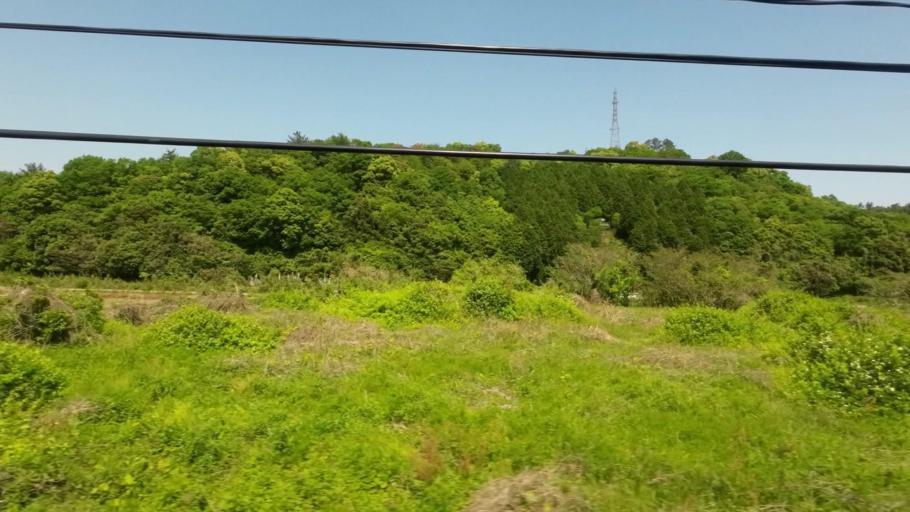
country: JP
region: Ehime
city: Niihama
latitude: 33.9337
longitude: 133.2731
